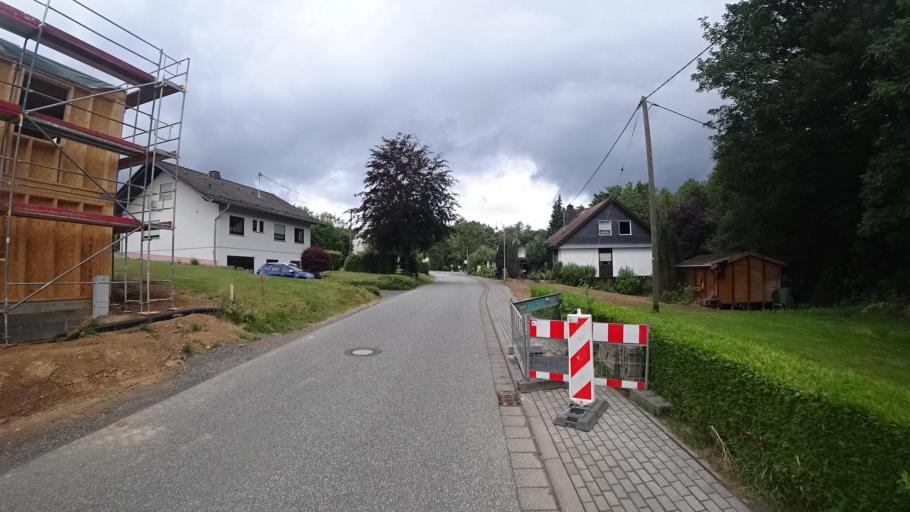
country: DE
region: Rheinland-Pfalz
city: Fiersbach
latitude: 50.7089
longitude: 7.5047
